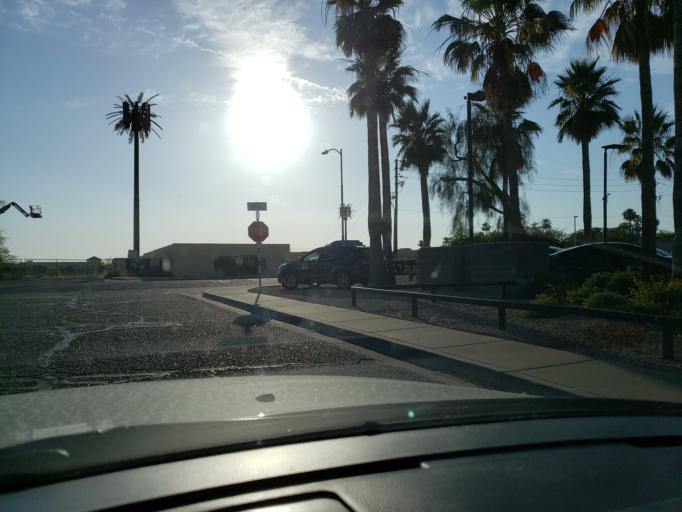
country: US
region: Arizona
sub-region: Maricopa County
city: Glendale
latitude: 33.6387
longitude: -112.0867
